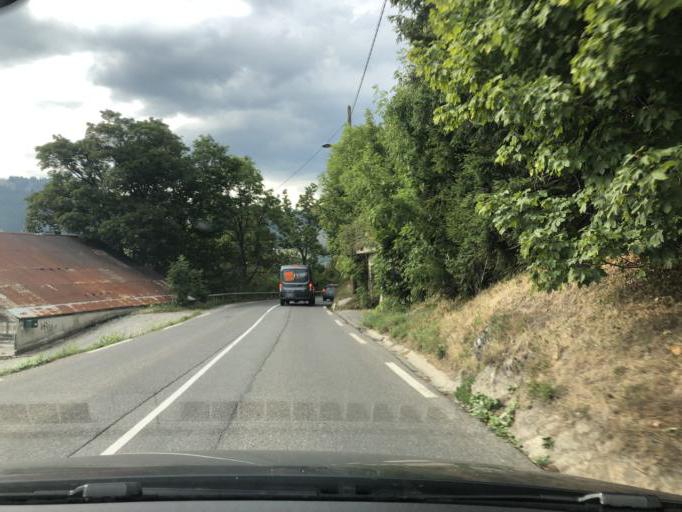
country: FR
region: Rhone-Alpes
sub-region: Departement de la Haute-Savoie
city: Megeve
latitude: 45.8599
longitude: 6.6305
